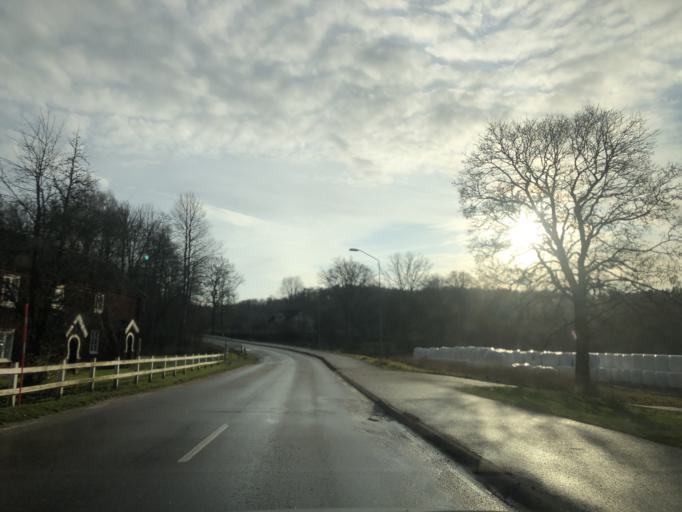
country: SE
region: Vaestra Goetaland
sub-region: Ulricehamns Kommun
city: Ulricehamn
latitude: 57.7361
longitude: 13.4248
